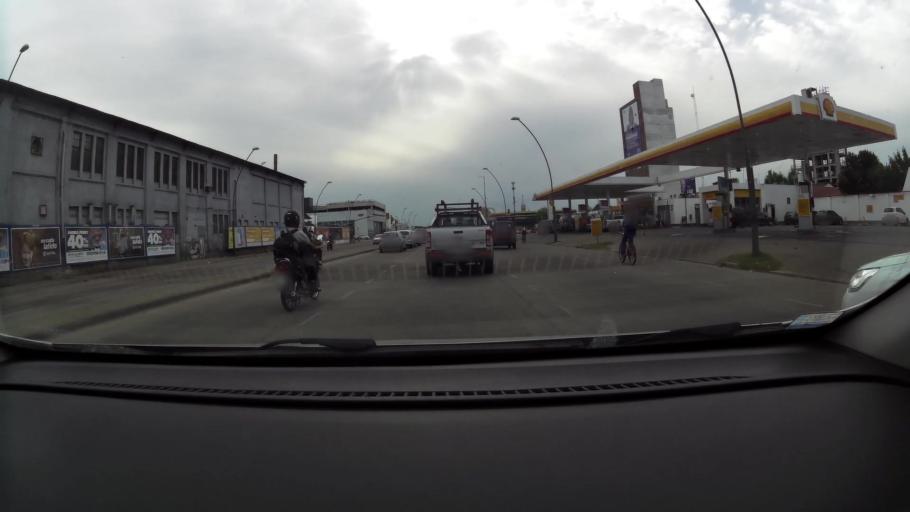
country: AR
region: Santa Fe
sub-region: Departamento de Rosario
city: Rosario
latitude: -32.9219
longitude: -60.6736
